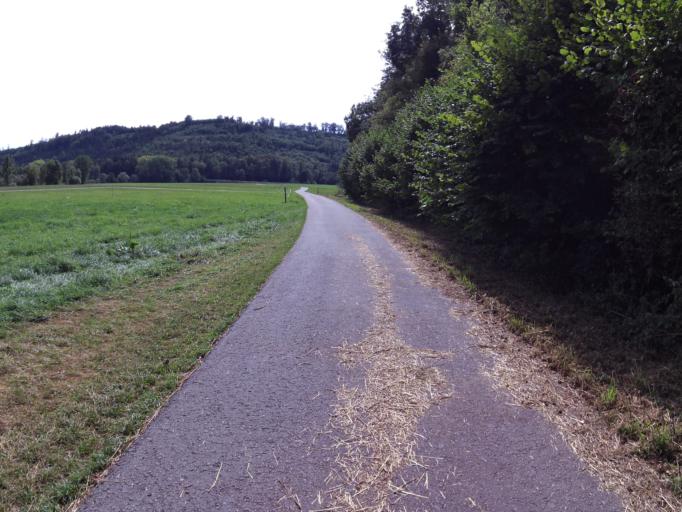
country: DE
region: Baden-Wuerttemberg
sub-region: Freiburg Region
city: Sulz am Neckar
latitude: 48.3999
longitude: 8.6409
